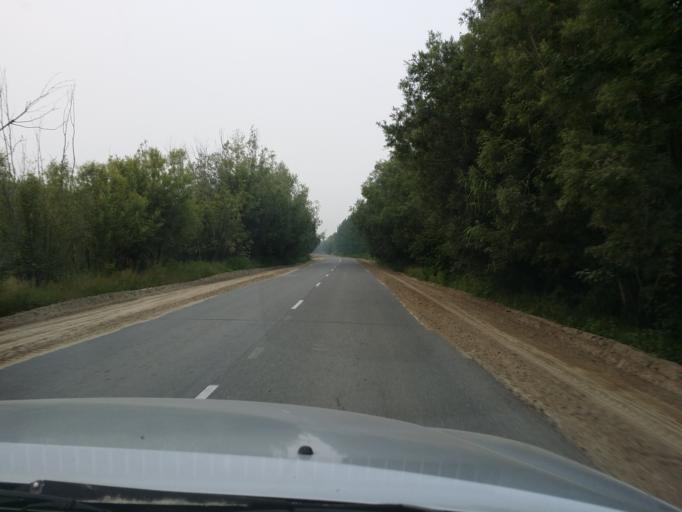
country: RU
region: Khanty-Mansiyskiy Avtonomnyy Okrug
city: Megion
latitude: 61.0042
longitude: 76.3084
